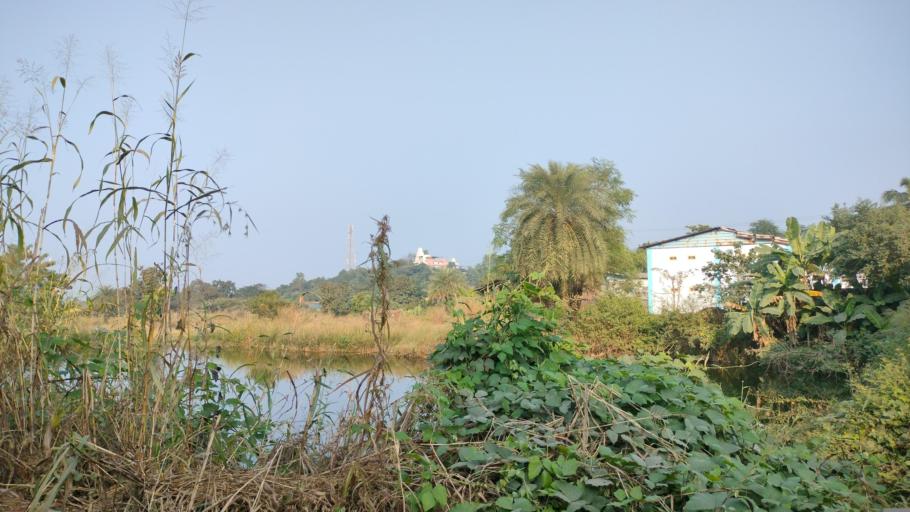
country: IN
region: Maharashtra
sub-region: Thane
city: Virar
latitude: 19.4616
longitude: 72.8816
